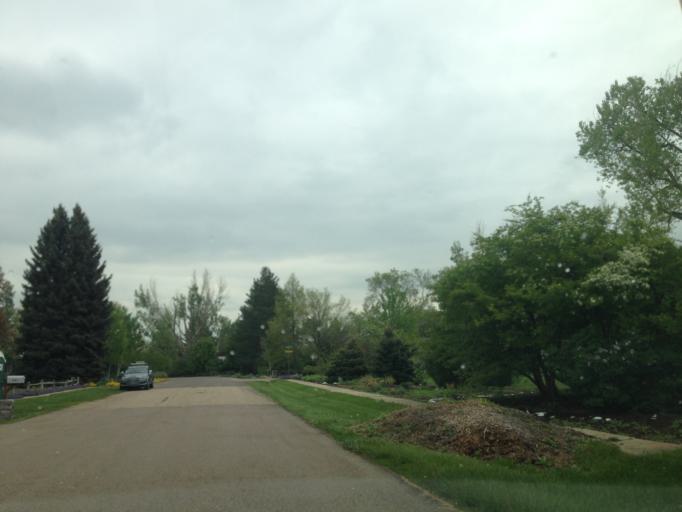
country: US
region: Colorado
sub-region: Boulder County
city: Louisville
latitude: 40.0027
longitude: -105.1712
